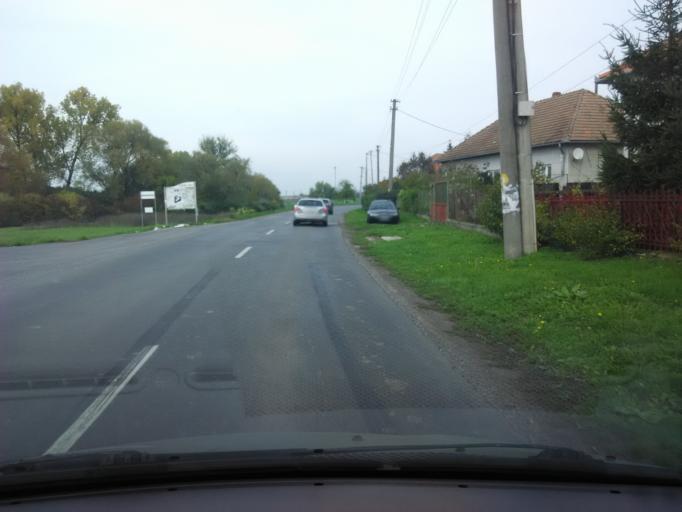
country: SK
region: Nitriansky
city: Levice
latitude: 48.1119
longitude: 18.5303
